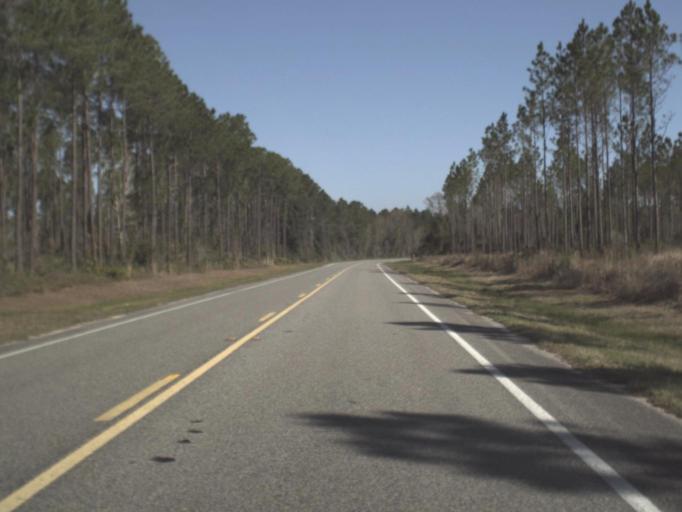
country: US
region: Florida
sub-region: Leon County
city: Woodville
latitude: 30.3058
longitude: -84.0477
